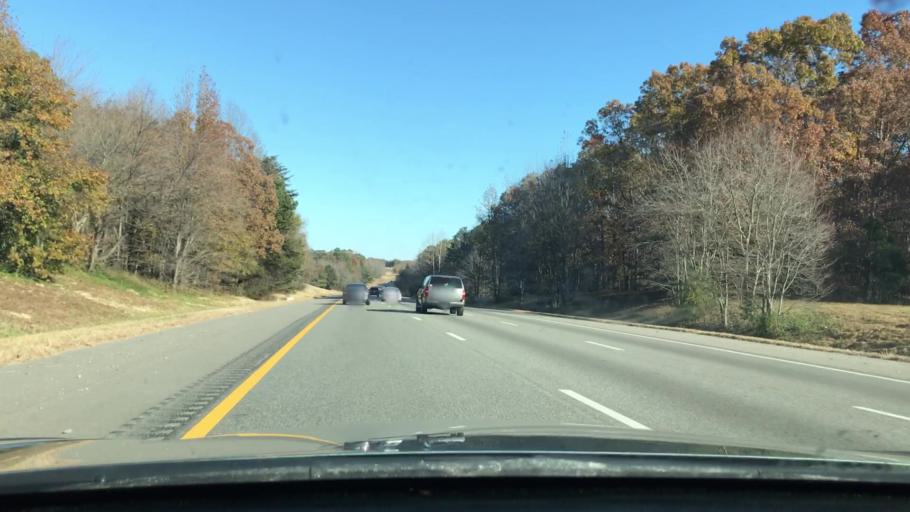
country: US
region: Virginia
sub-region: Henrico County
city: Glen Allen
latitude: 37.6807
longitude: -77.5384
